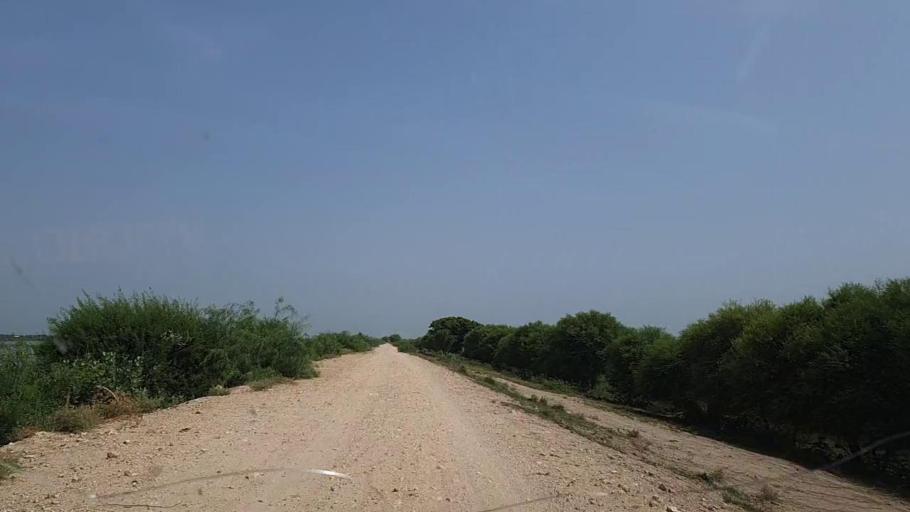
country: PK
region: Sindh
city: Ghotki
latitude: 28.0986
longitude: 69.4027
